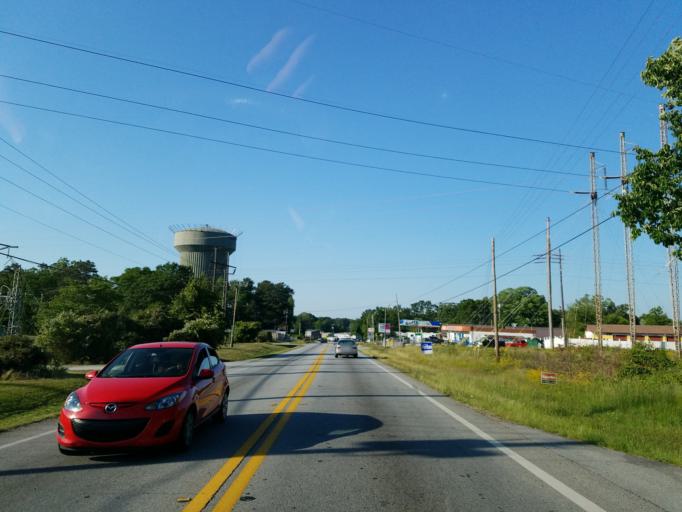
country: US
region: Georgia
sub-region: Douglas County
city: Lithia Springs
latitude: 33.7811
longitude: -84.7034
